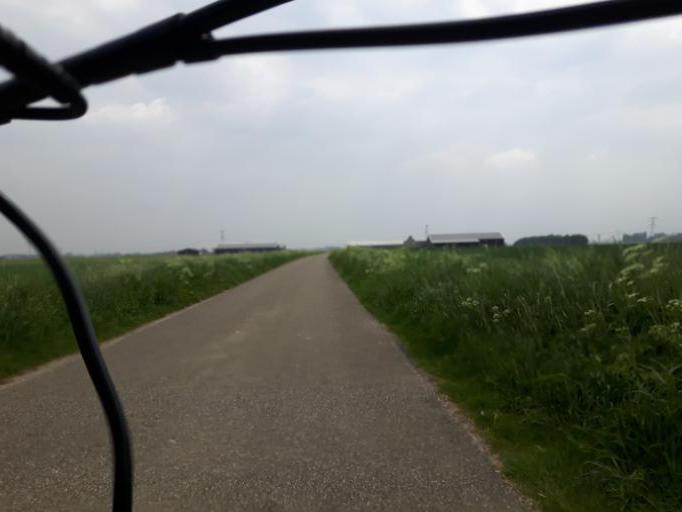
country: NL
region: North Brabant
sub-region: Gemeente Steenbergen
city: Kruisland
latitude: 51.5663
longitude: 4.3928
